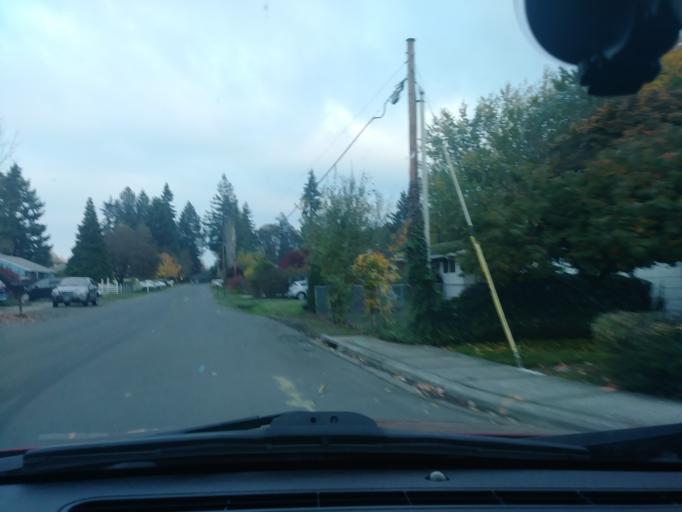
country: US
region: Oregon
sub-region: Washington County
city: Aloha
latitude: 45.4869
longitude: -122.8517
